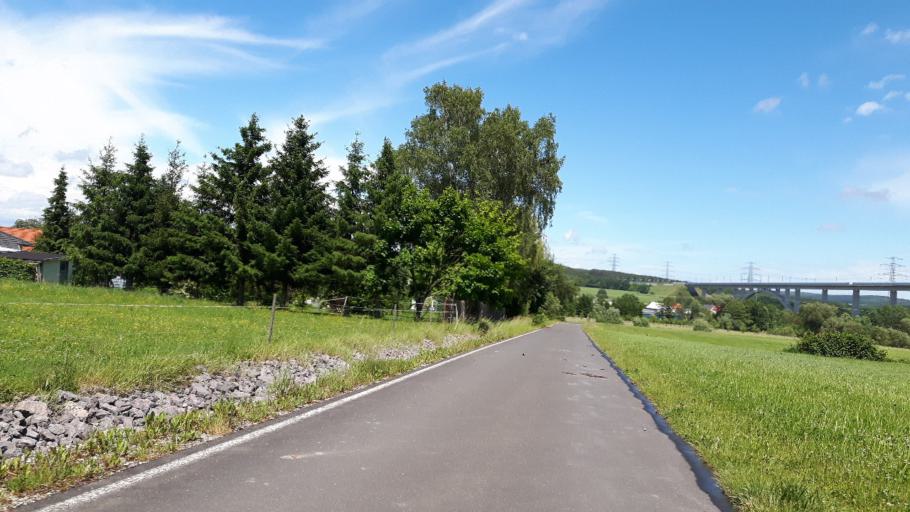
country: DE
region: Thuringia
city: Langewiesen
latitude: 50.6667
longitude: 10.9801
